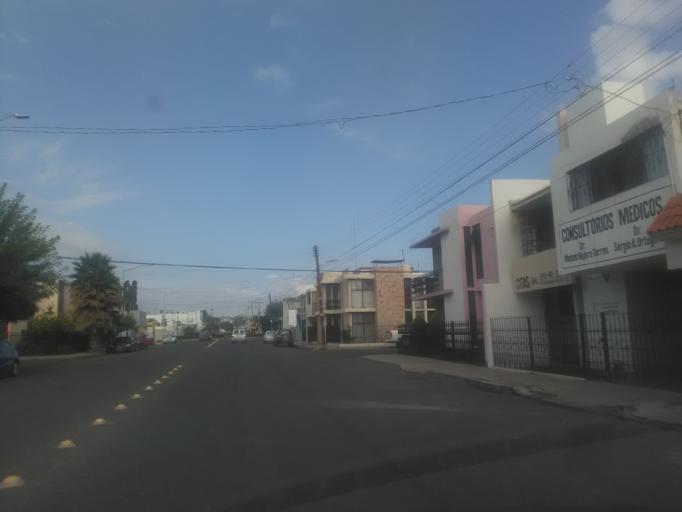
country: MX
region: Durango
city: Victoria de Durango
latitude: 24.0278
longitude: -104.6476
